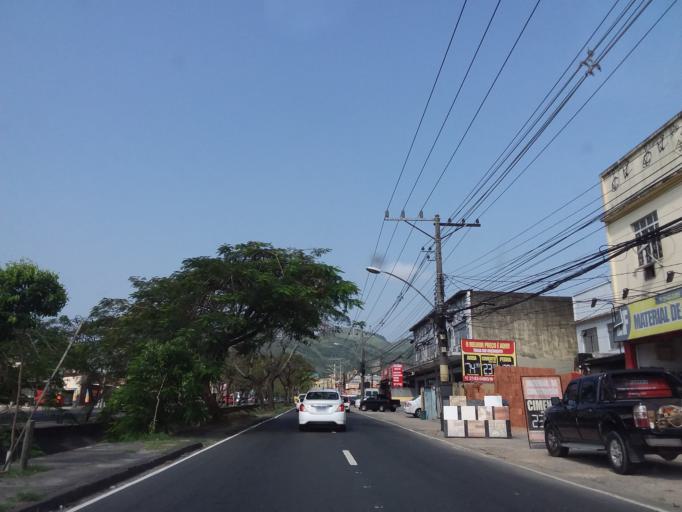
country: BR
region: Rio de Janeiro
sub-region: Nilopolis
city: Nilopolis
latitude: -22.9023
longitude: -43.5484
